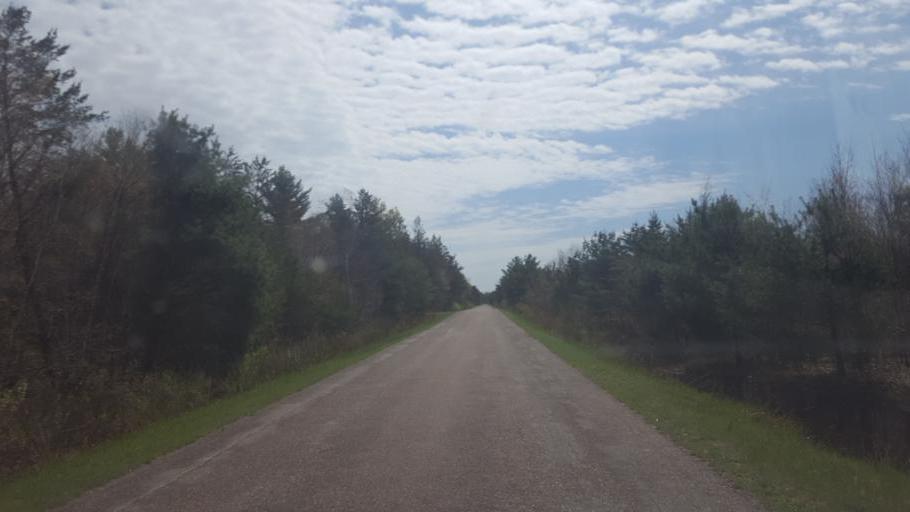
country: US
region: Wisconsin
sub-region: Clark County
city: Neillsville
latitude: 44.3019
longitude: -90.4895
